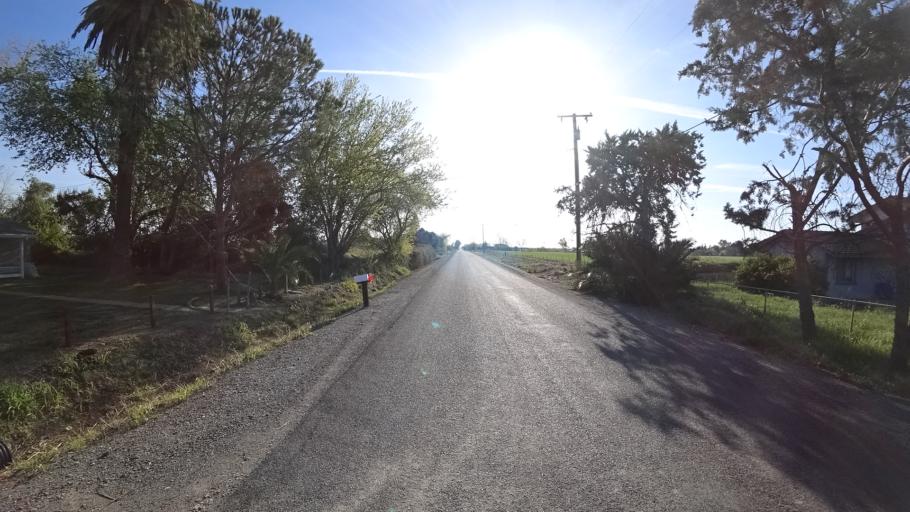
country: US
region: California
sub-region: Glenn County
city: Orland
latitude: 39.7257
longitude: -122.2199
